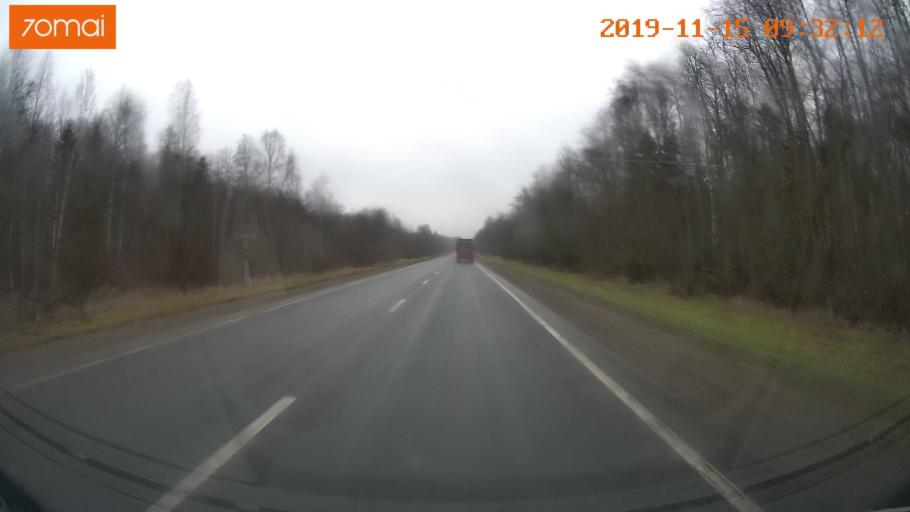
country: RU
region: Vologda
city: Sheksna
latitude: 59.2725
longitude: 38.3284
